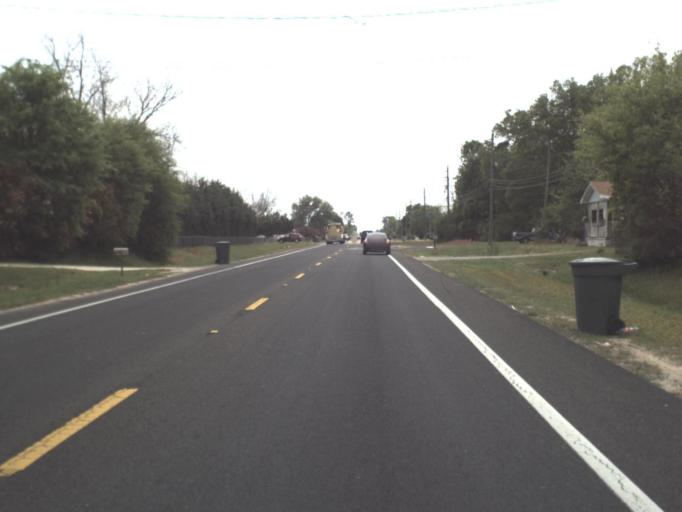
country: US
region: Florida
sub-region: Escambia County
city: Bellview
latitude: 30.4756
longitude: -87.3237
